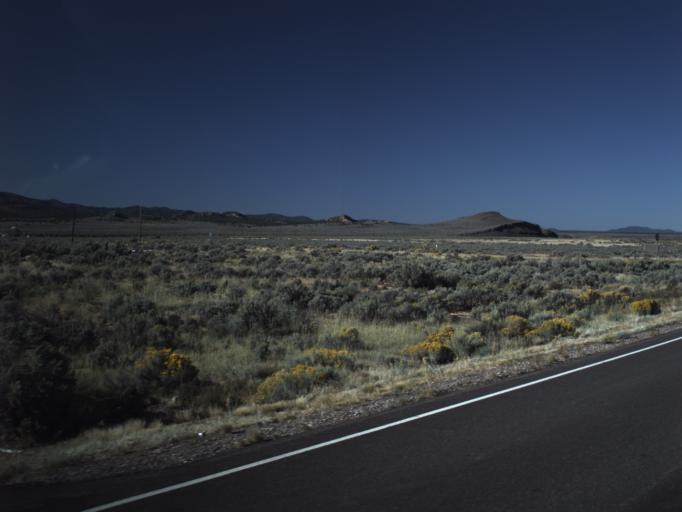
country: US
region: Utah
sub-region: Washington County
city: Enterprise
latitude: 37.8027
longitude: -113.9245
